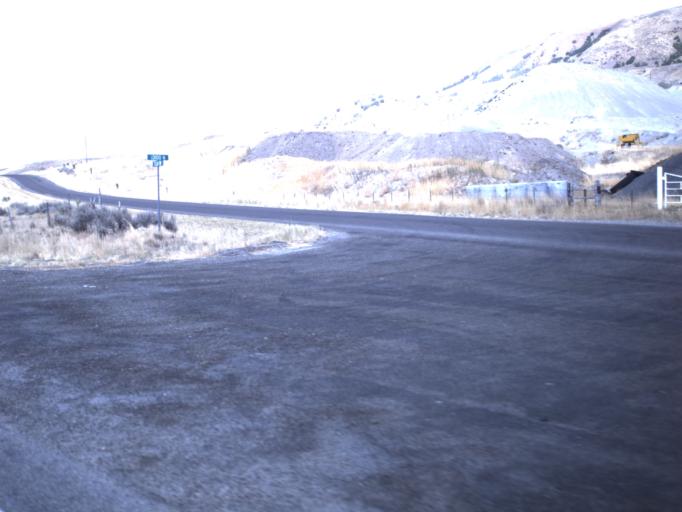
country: US
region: Utah
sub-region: Box Elder County
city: Garland
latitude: 41.7457
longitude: -112.0995
